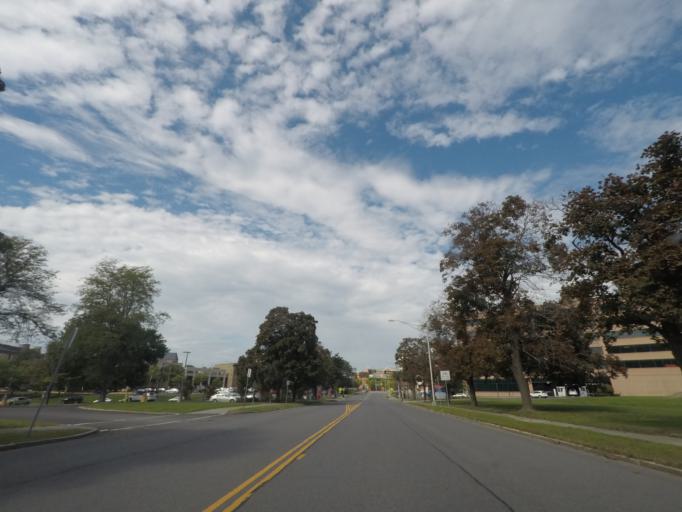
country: US
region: New York
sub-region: Albany County
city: Albany
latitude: 42.6504
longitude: -73.7753
